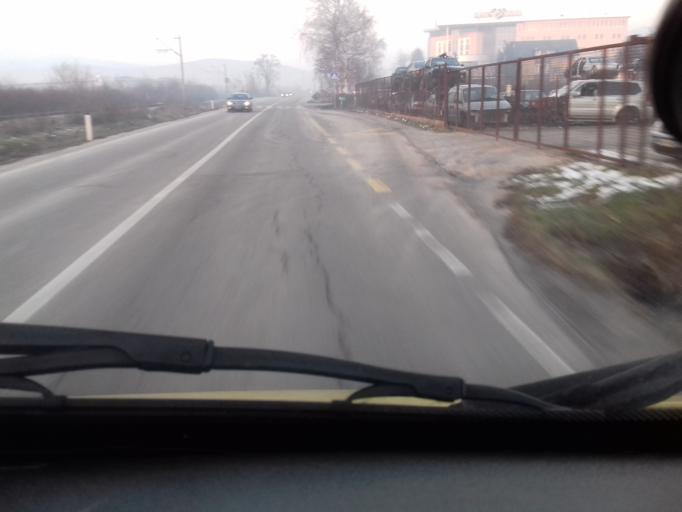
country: BA
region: Federation of Bosnia and Herzegovina
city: Vogosca
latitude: 43.8753
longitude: 18.3120
